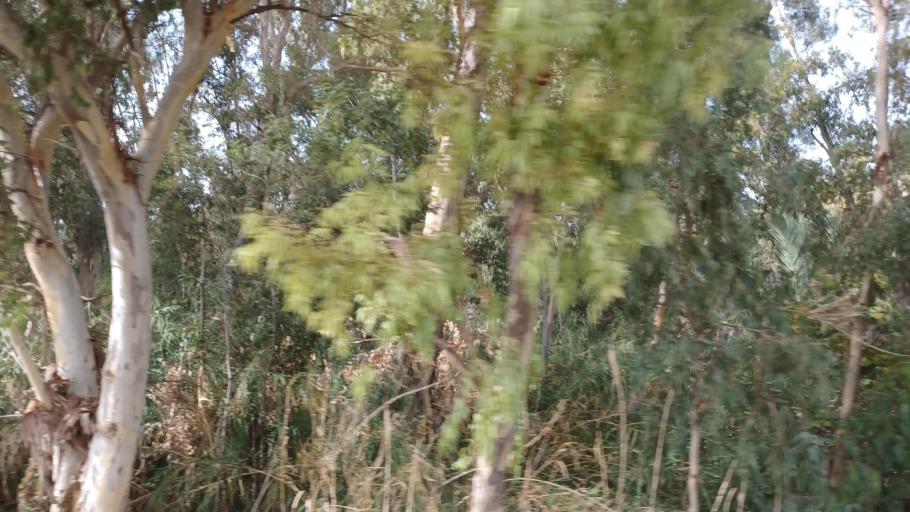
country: CY
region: Pafos
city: Polis
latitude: 35.0411
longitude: 32.4195
